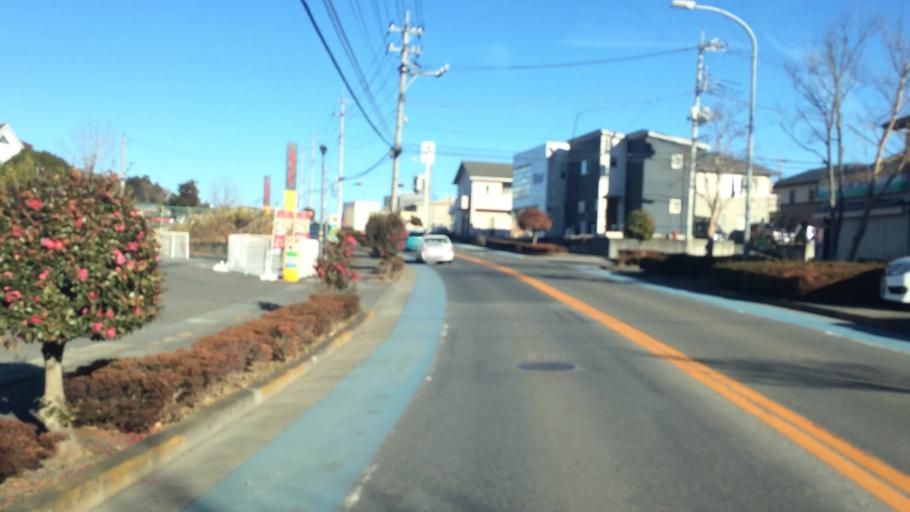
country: JP
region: Tochigi
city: Utsunomiya-shi
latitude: 36.5703
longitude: 139.9368
